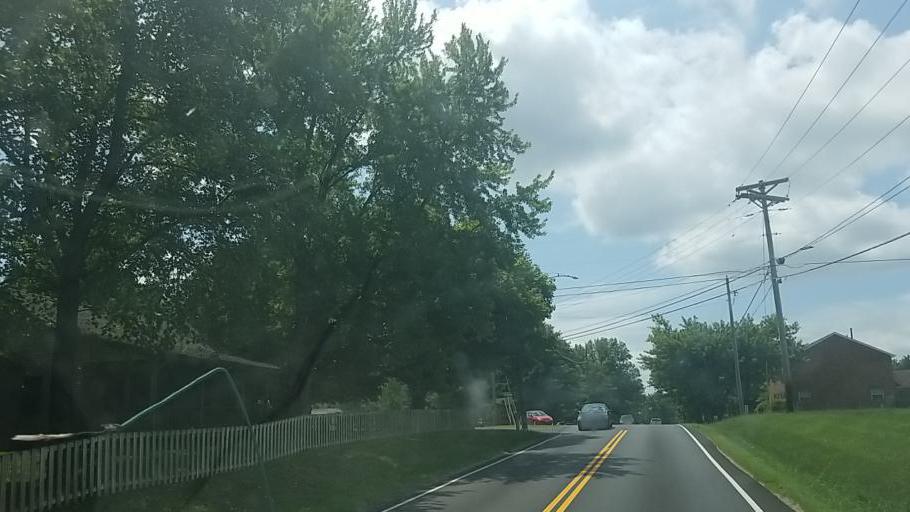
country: US
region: Ohio
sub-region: Fairfield County
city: Pickerington
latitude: 39.8897
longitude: -82.7501
